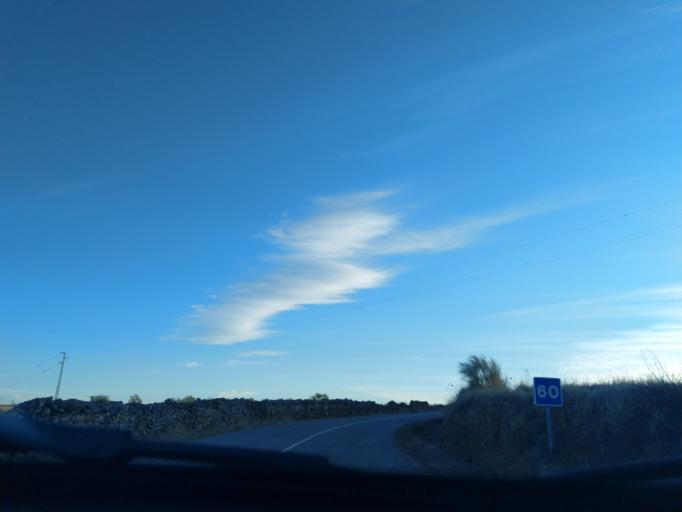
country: ES
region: Extremadura
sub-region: Provincia de Badajoz
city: Valverde de Llerena
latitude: 38.2129
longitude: -5.8254
